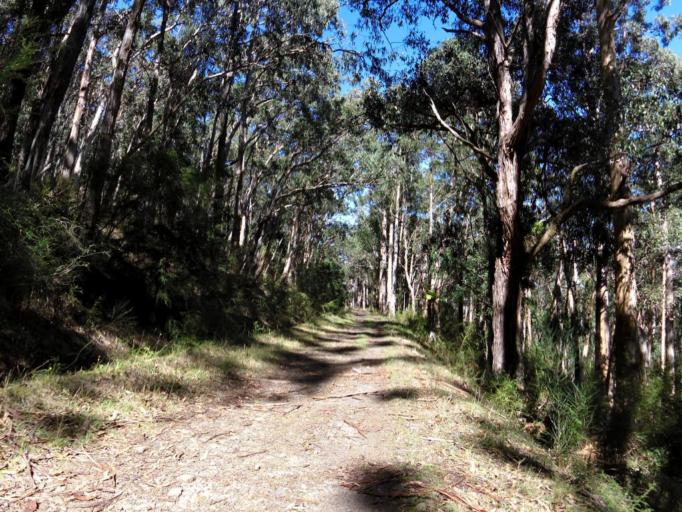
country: AU
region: Victoria
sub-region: Yarra Ranges
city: Yarra Junction
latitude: -37.7388
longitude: 145.5970
